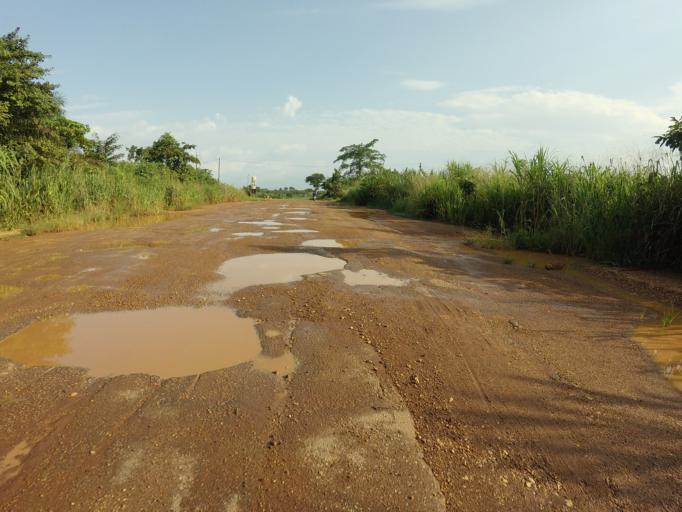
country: GH
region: Volta
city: Hohoe
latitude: 7.0893
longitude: 0.4451
